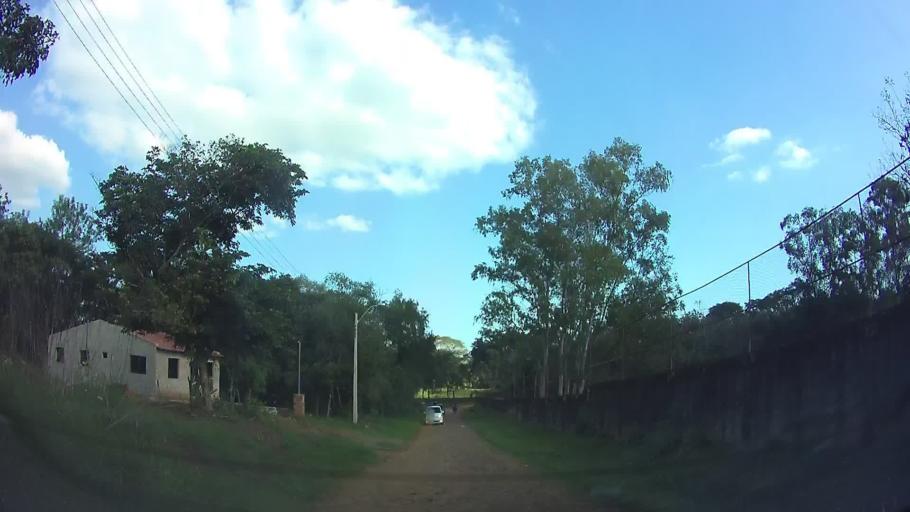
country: PY
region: Central
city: Capiata
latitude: -25.2775
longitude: -57.4554
